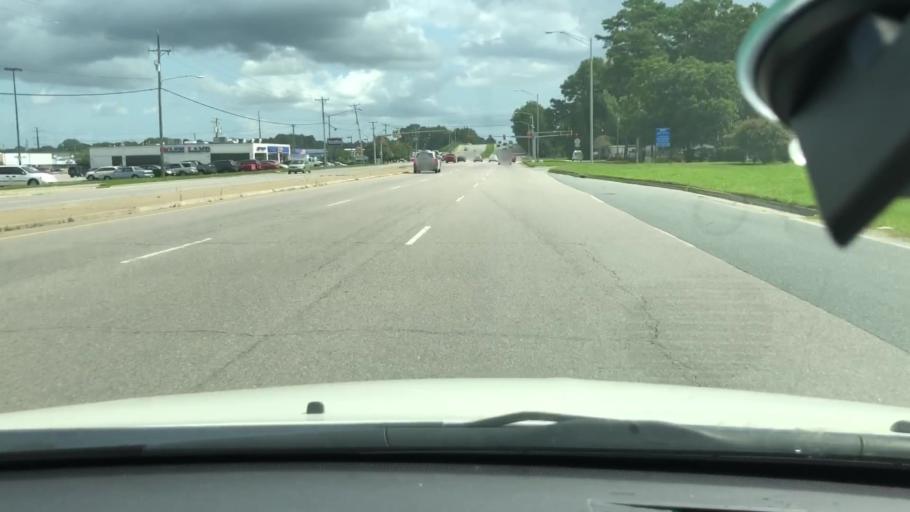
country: US
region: Virginia
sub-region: City of Chesapeake
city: Chesapeake
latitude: 36.7840
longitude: -76.2567
